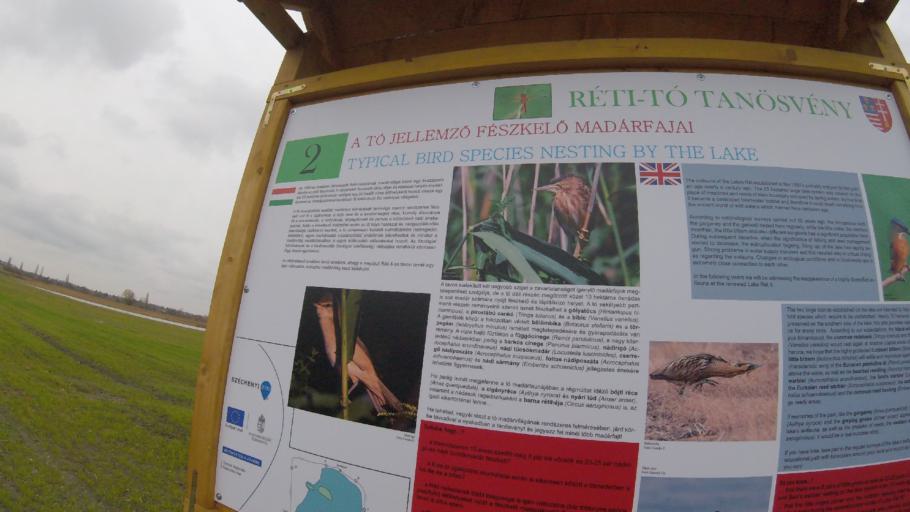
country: HU
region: Komarom-Esztergom
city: Tata
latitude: 47.6563
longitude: 18.3058
